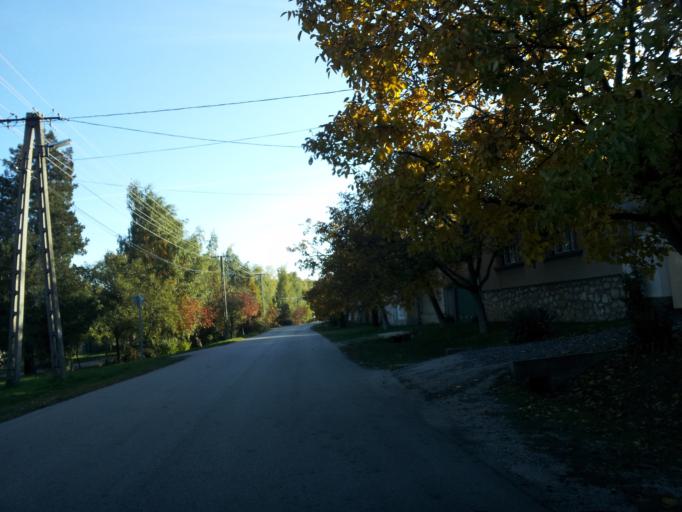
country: HU
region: Gyor-Moson-Sopron
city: Bakonyszentlaszlo
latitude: 47.3854
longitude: 17.8003
